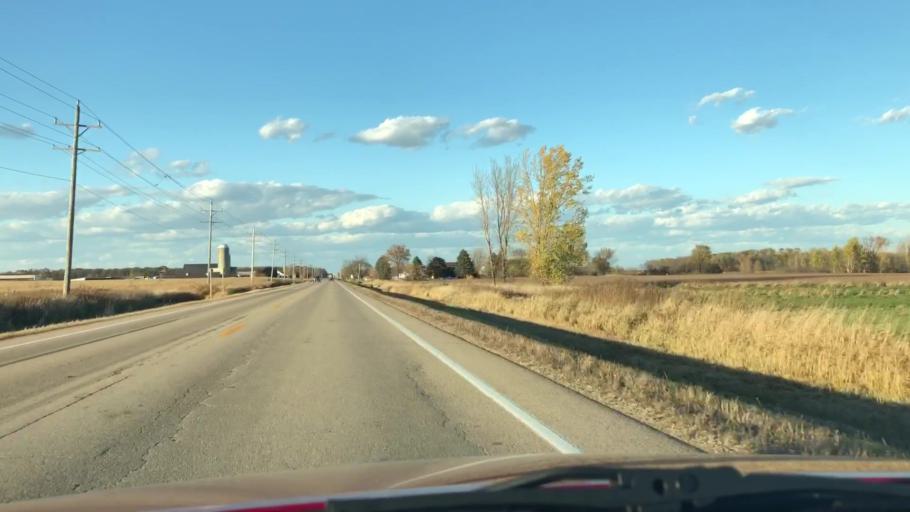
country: US
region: Wisconsin
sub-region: Outagamie County
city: Seymour
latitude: 44.4447
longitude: -88.2912
